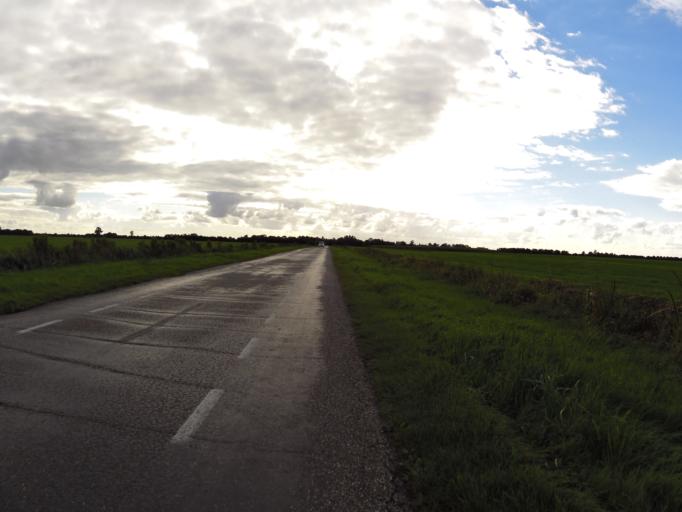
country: NL
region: Utrecht
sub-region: Stichtse Vecht
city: Breukelen
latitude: 52.1405
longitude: 4.9426
